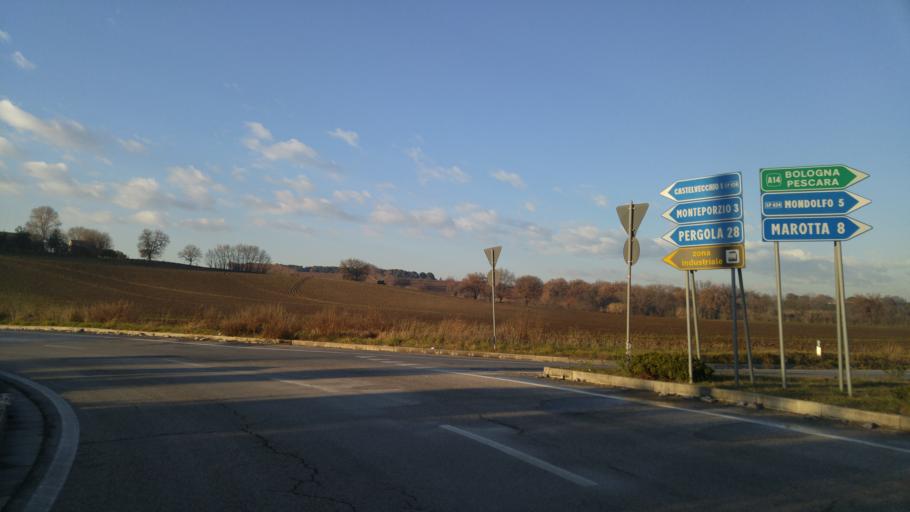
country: IT
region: The Marches
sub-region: Provincia di Ancona
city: Monterado
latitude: 43.7103
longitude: 13.0749
